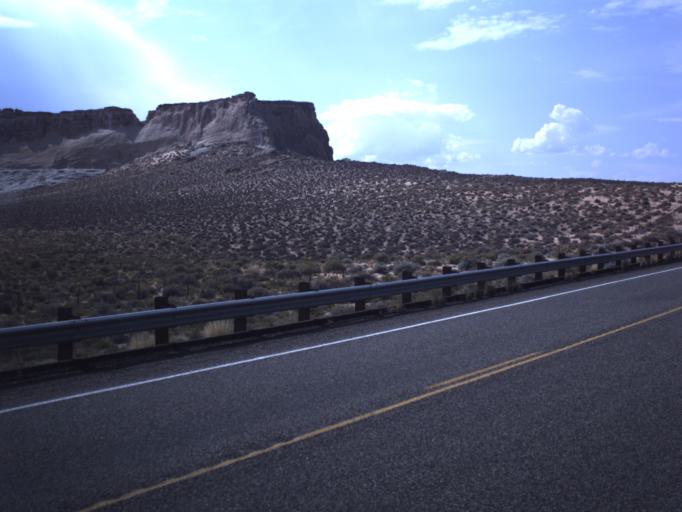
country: US
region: Arizona
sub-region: Coconino County
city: Page
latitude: 37.0296
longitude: -111.6039
